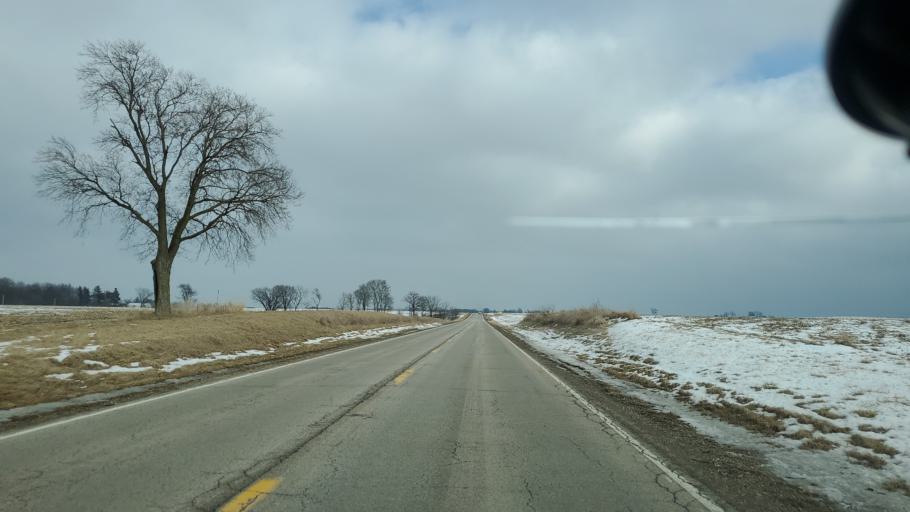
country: US
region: Illinois
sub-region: Marshall County
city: Toluca
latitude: 41.1185
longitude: -89.1910
